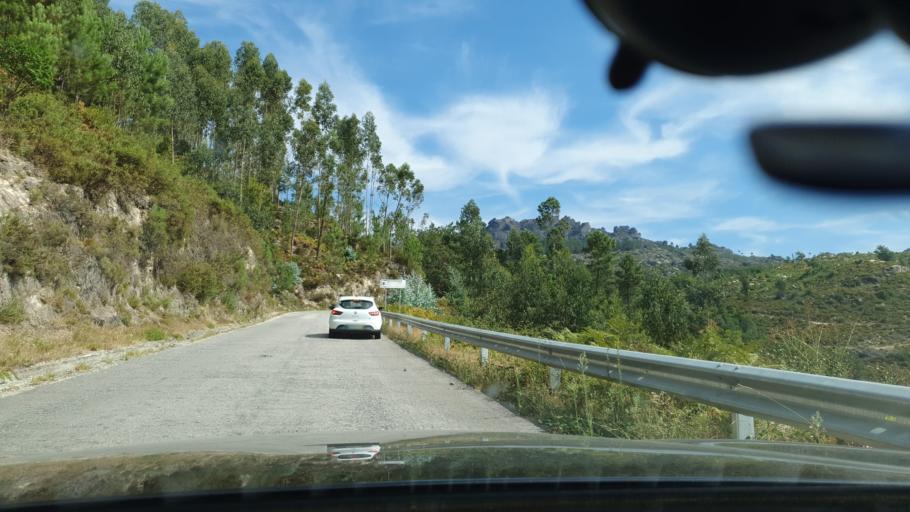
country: PT
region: Braga
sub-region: Vieira do Minho
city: Vieira do Minho
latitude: 41.6981
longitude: -8.0836
